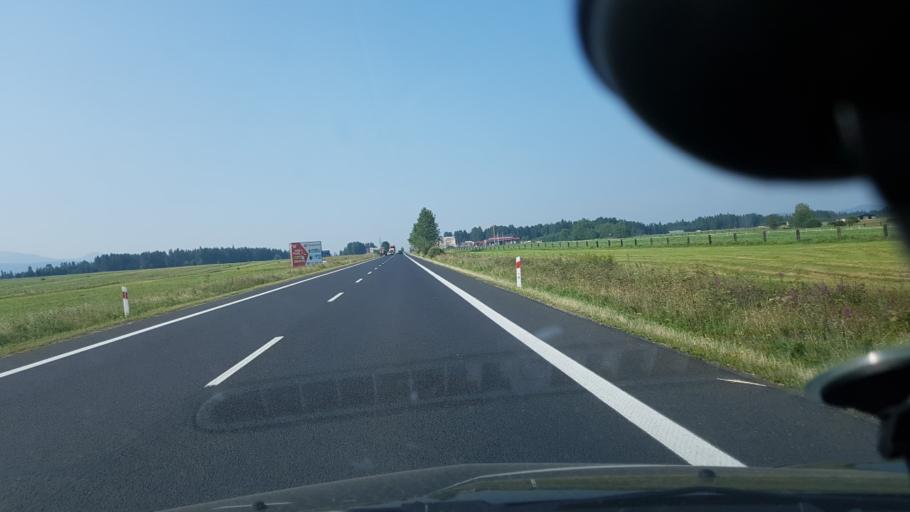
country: PL
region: Lesser Poland Voivodeship
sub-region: Powiat nowotarski
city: Chyzne
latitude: 49.4220
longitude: 19.6706
